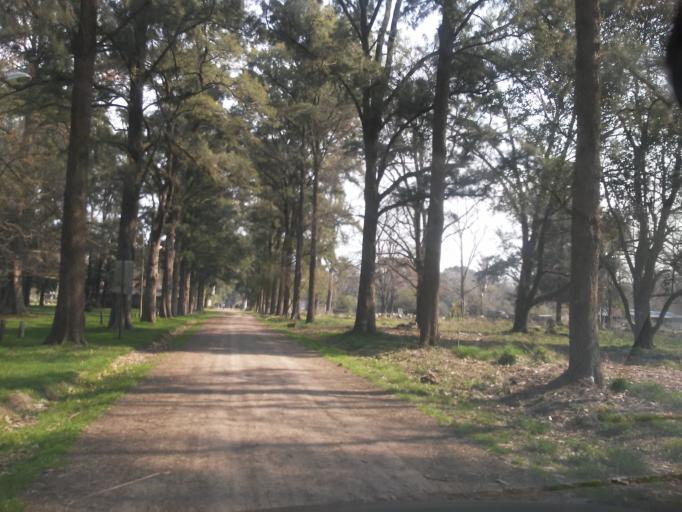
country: AR
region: Buenos Aires
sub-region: Partido de General Rodriguez
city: General Rodriguez
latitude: -34.6642
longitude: -58.8592
